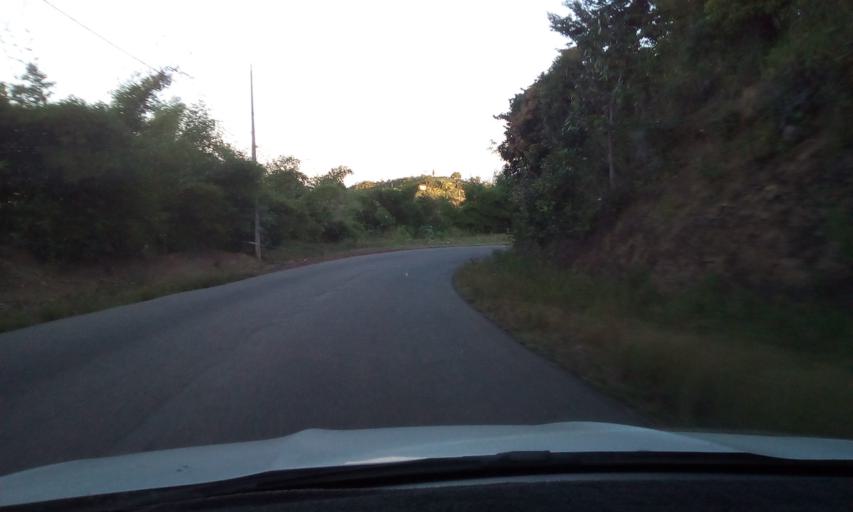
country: BR
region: Paraiba
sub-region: Areia
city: Areia
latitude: -6.9735
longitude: -35.6901
